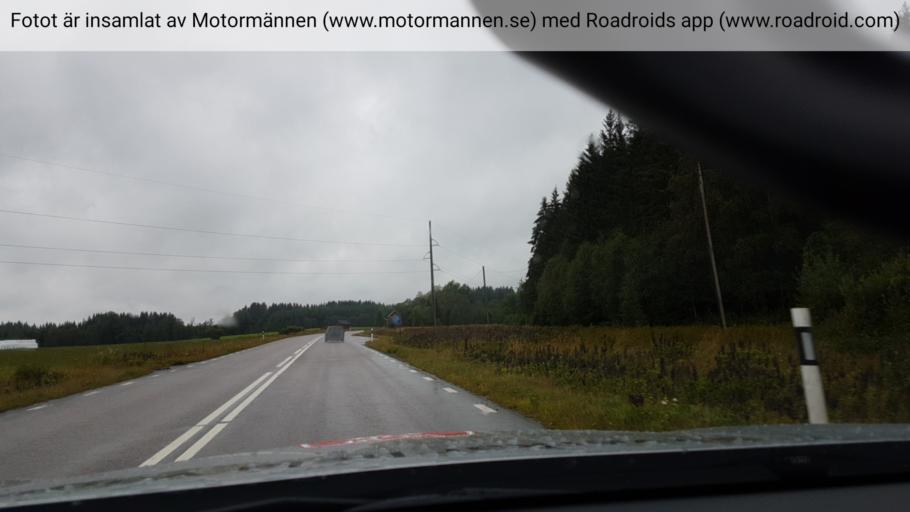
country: SE
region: Vaestra Goetaland
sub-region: Dals-Ed Kommun
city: Ed
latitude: 58.8894
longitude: 11.9177
